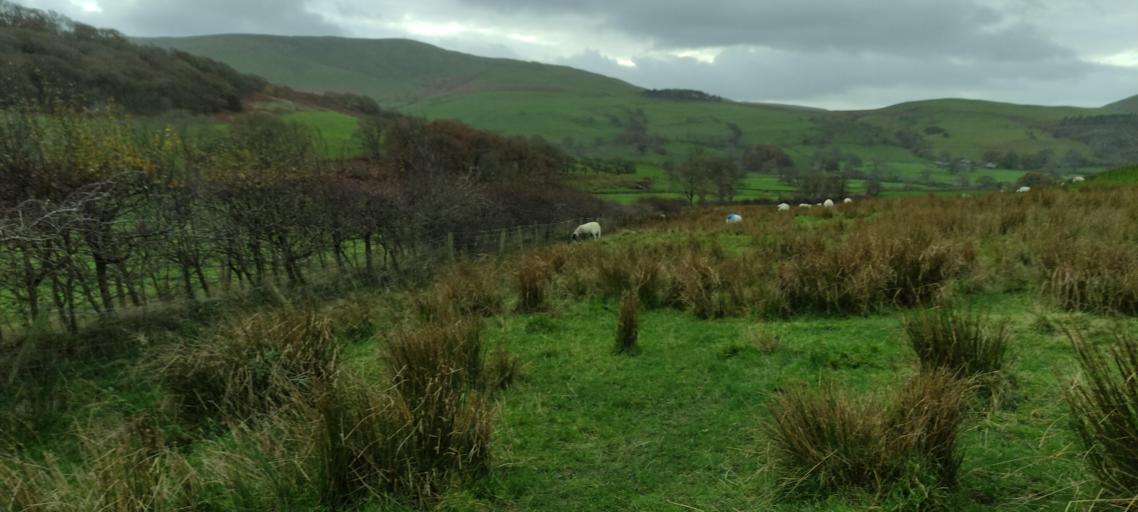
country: GB
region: England
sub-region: Cumbria
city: Keswick
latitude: 54.6511
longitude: -3.2331
